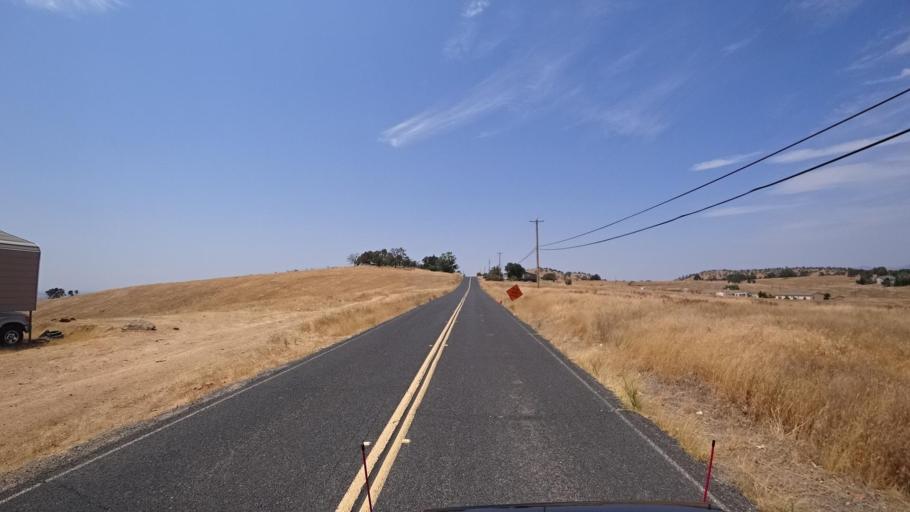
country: US
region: California
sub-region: Tuolumne County
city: Jamestown
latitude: 37.6518
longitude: -120.3408
